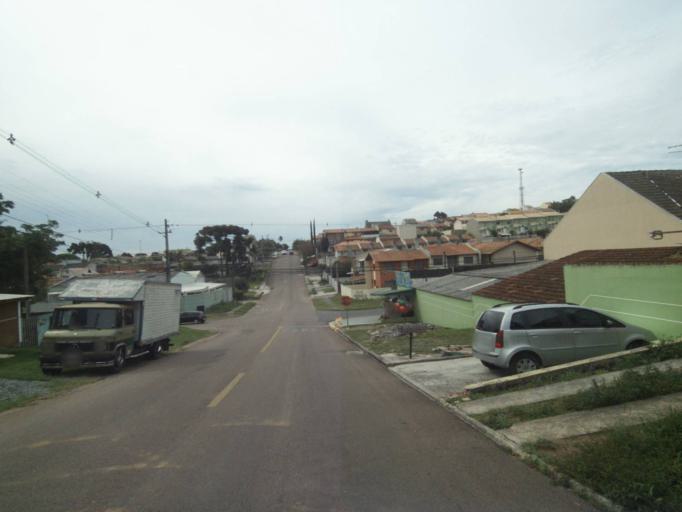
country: BR
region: Parana
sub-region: Pinhais
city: Pinhais
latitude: -25.4186
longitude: -49.2086
